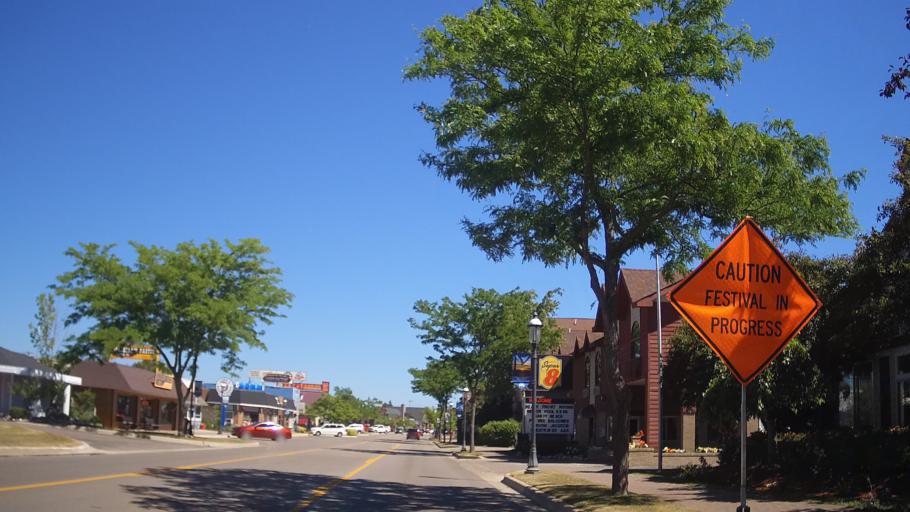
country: US
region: Michigan
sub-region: Mackinac County
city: Saint Ignace
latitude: 45.7758
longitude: -84.7266
